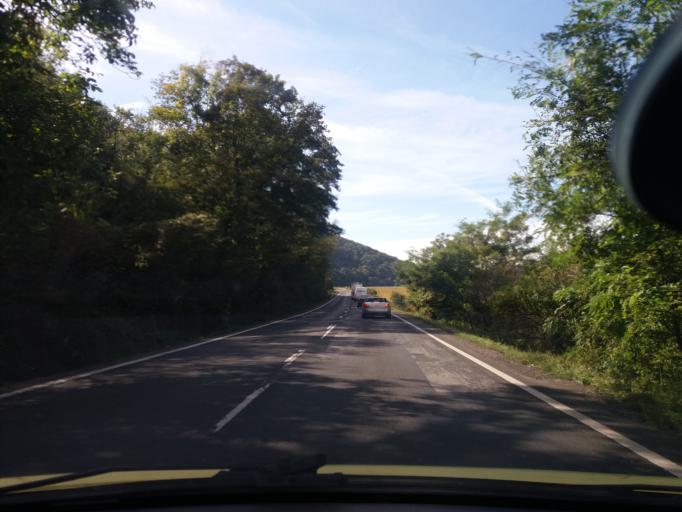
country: RO
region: Hunedoara
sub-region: Comuna Branisca
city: Branisca
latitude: 45.9199
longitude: 22.7179
